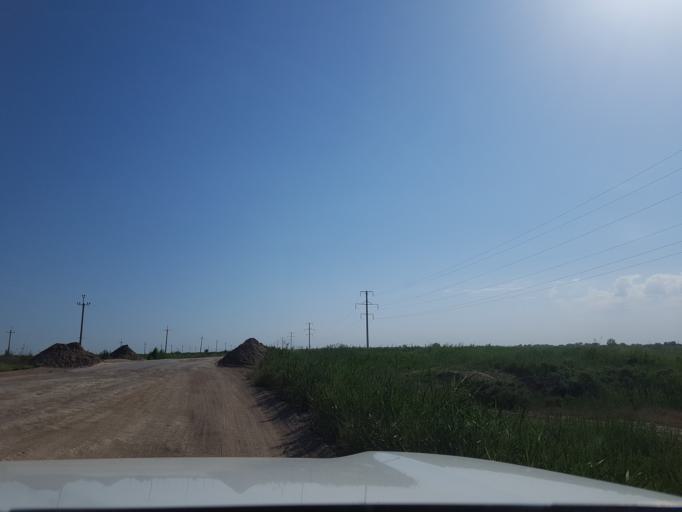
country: TM
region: Dasoguz
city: Koeneuergench
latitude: 42.1127
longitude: 58.9203
